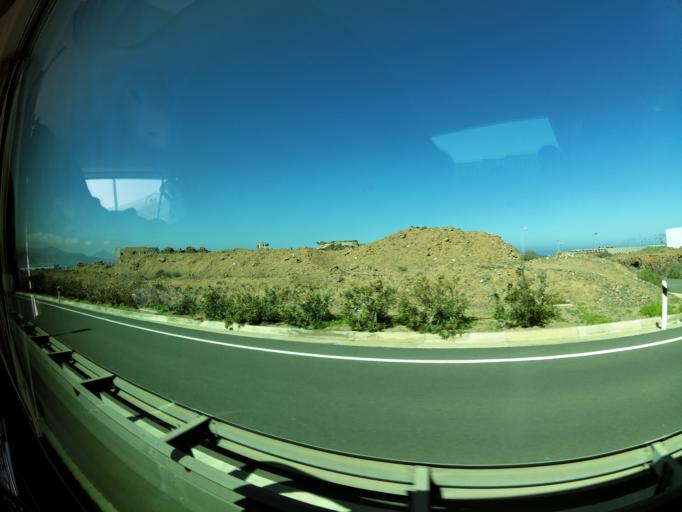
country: ES
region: Canary Islands
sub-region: Provincia de Las Palmas
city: Arucas
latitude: 28.1518
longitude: -15.5286
